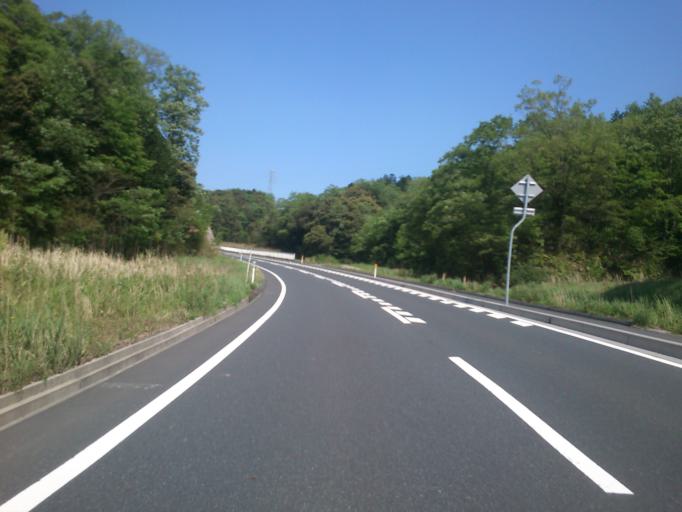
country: JP
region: Kyoto
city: Miyazu
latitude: 35.6719
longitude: 135.0761
